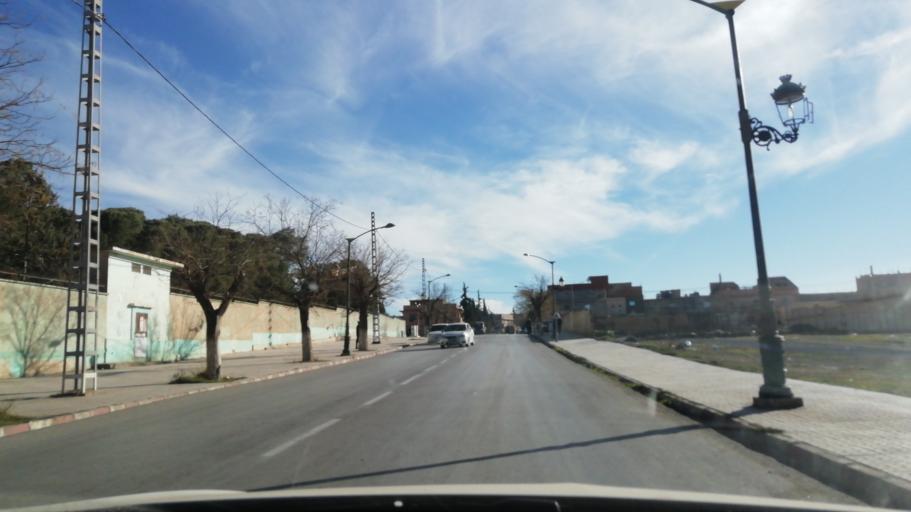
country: DZ
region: Tlemcen
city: Sebdou
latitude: 34.6347
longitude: -1.3334
